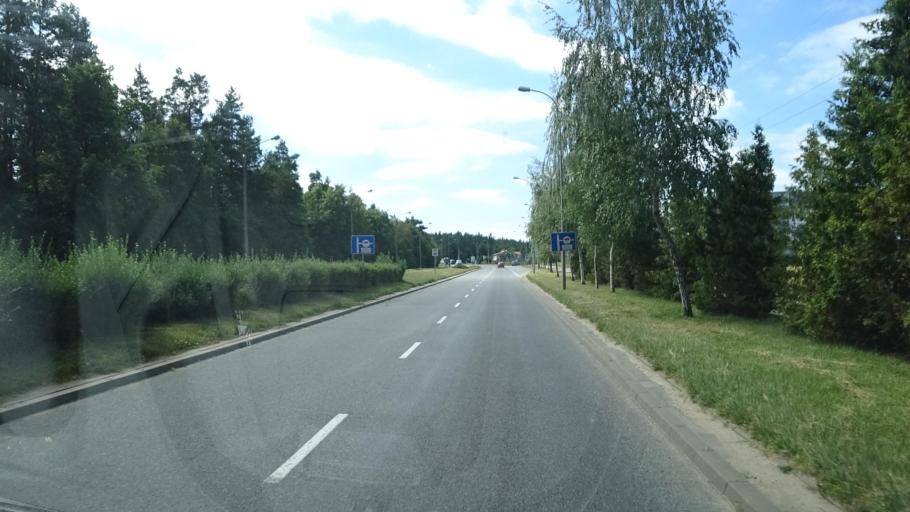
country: PL
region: Warmian-Masurian Voivodeship
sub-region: Powiat elcki
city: Elk
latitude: 53.7974
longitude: 22.3584
